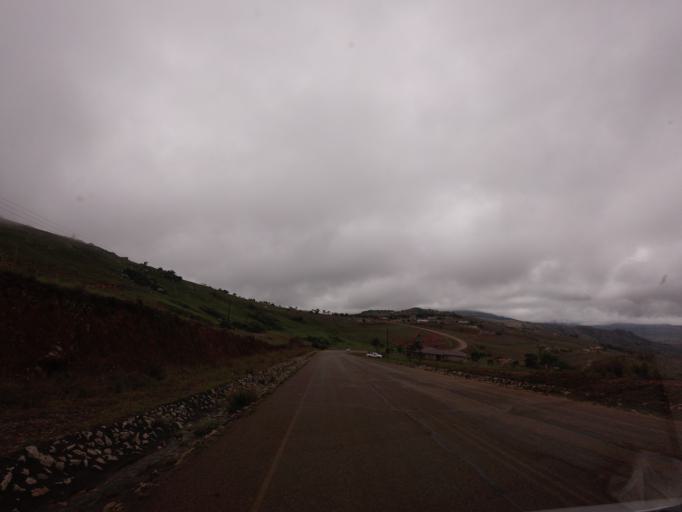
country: SZ
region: Hhohho
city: Piggs Peak
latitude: -26.1336
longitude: 31.2274
